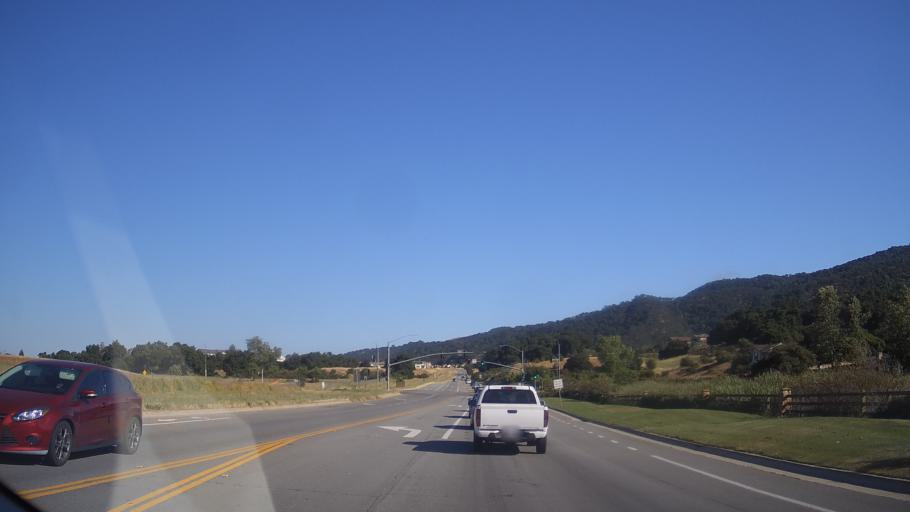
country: US
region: California
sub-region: Santa Clara County
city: Gilroy
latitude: 37.0025
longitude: -121.6001
